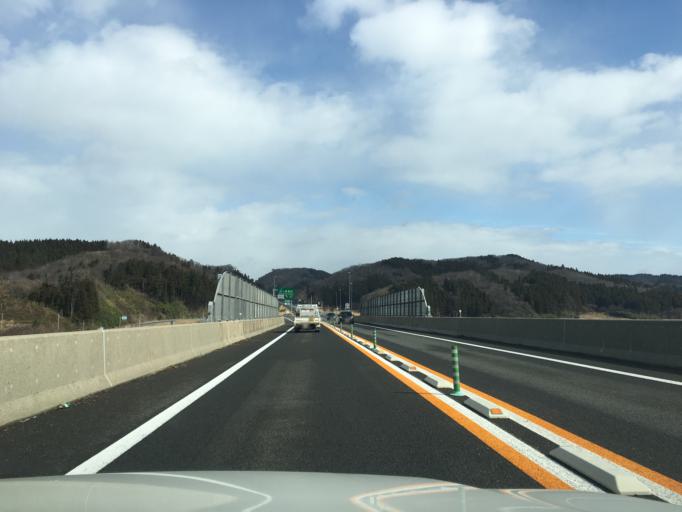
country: JP
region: Akita
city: Akita Shi
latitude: 39.4964
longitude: 140.0591
